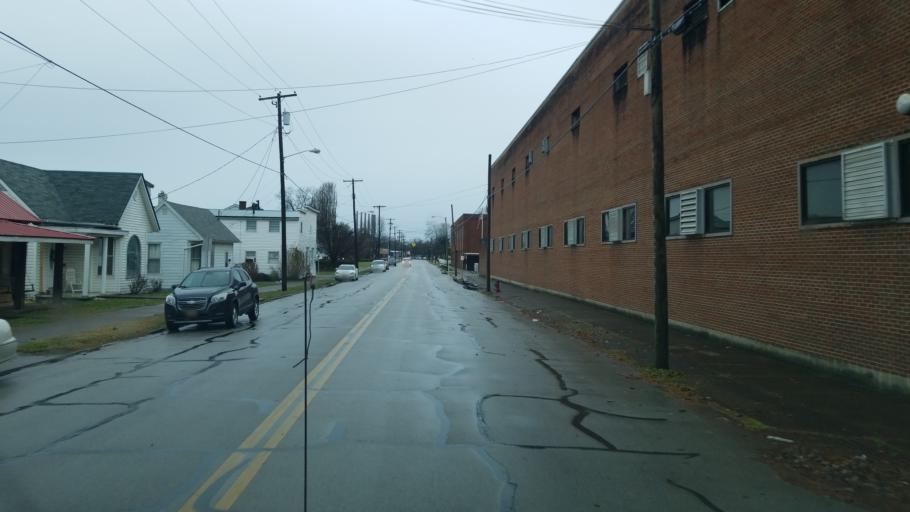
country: US
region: Kentucky
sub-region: Mason County
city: Maysville
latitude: 38.6429
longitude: -83.7395
